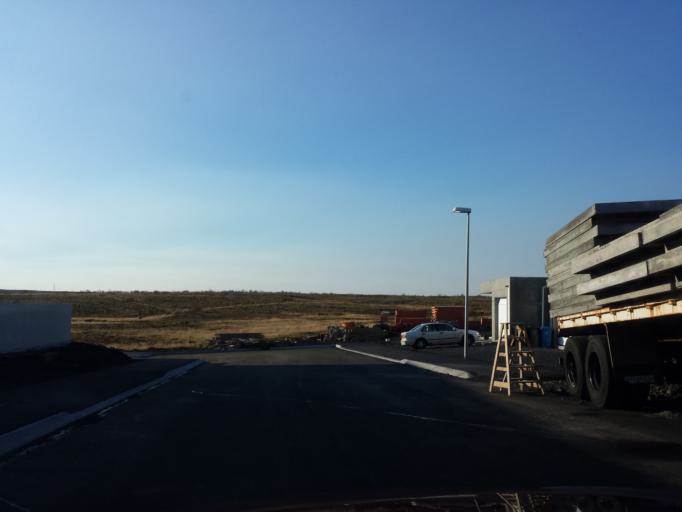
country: IS
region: Capital Region
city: Reykjavik
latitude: 64.0852
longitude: -21.8509
